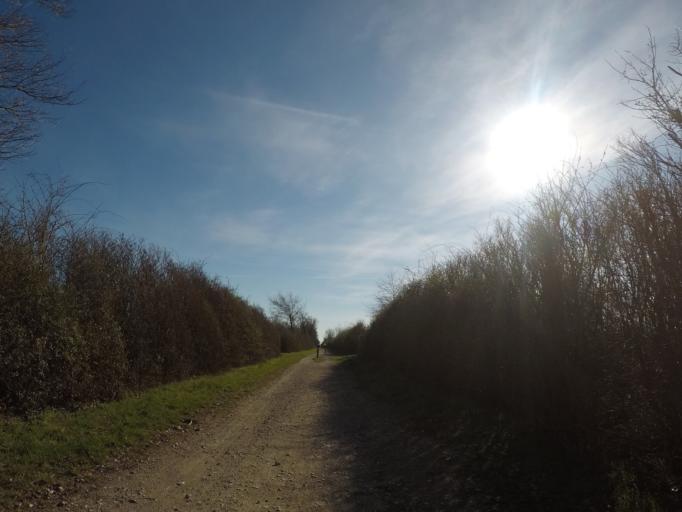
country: AT
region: Lower Austria
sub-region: Politischer Bezirk Modling
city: Vosendorf
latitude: 48.1125
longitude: 16.3460
